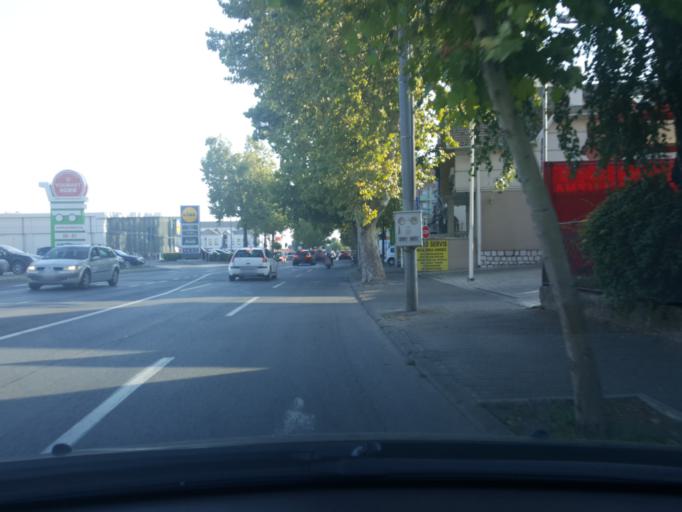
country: RS
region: Central Serbia
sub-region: Macvanski Okrug
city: Sabac
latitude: 44.7503
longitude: 19.7055
